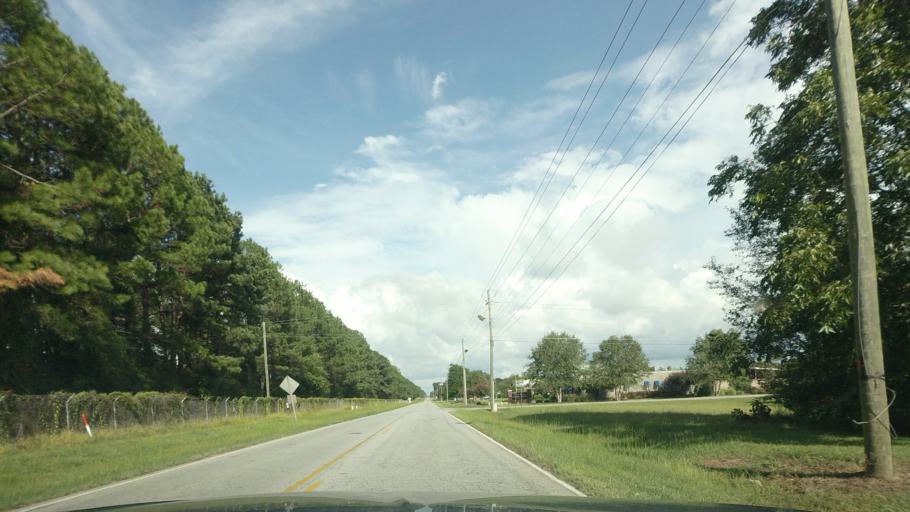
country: US
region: Georgia
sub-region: Peach County
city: Byron
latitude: 32.6515
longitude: -83.7419
